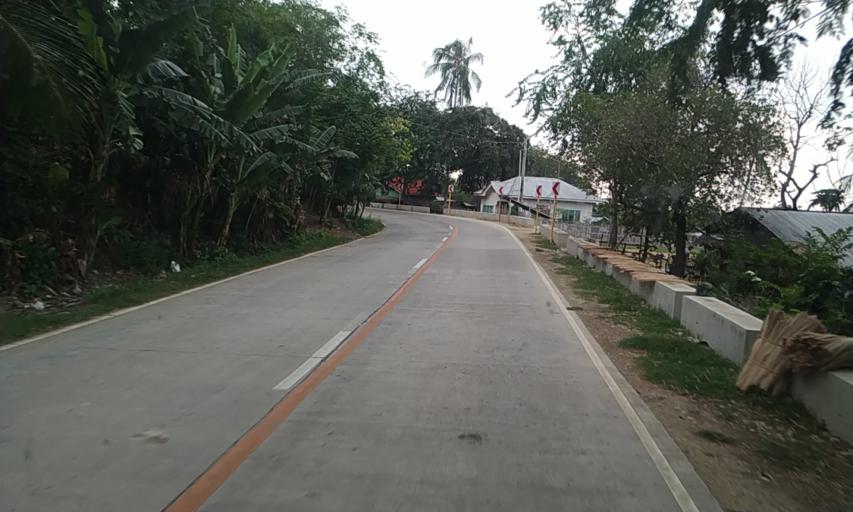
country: PH
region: Central Visayas
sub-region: Province of Negros Oriental
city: Calamba
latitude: 10.1972
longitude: 123.2973
